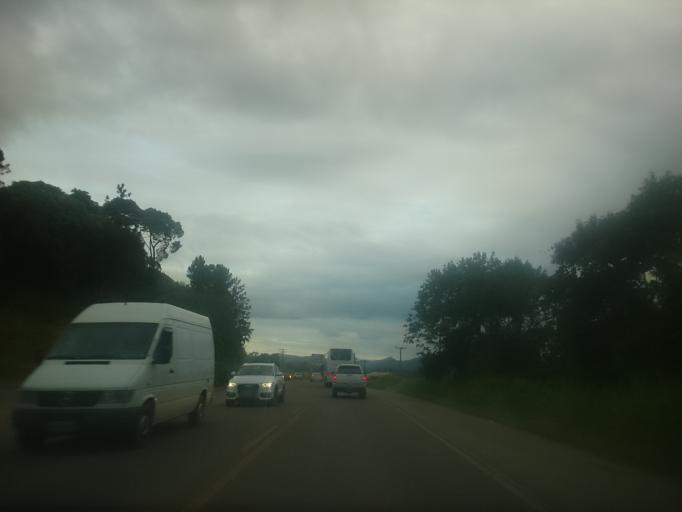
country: BR
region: Santa Catarina
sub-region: Gaspar
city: Gaspar
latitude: -26.9110
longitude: -48.9784
